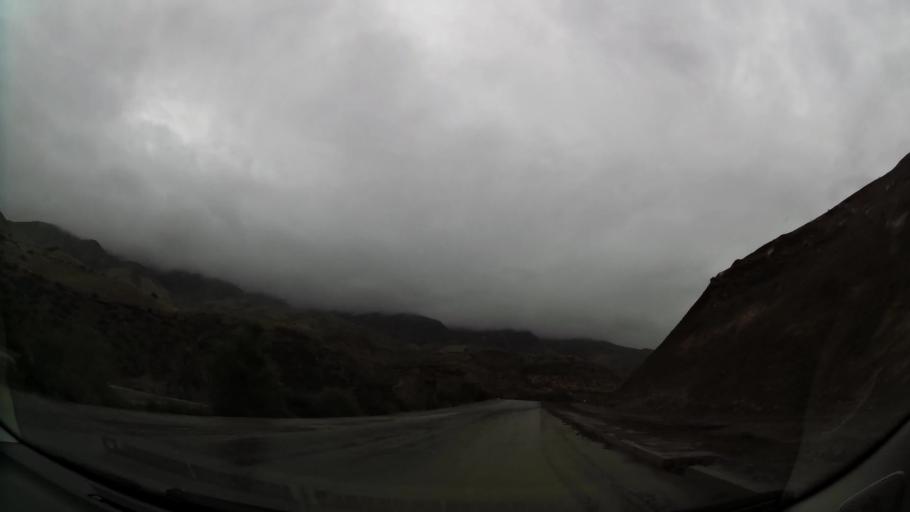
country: MA
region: Taza-Al Hoceima-Taounate
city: Imzourene
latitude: 35.0084
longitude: -3.8141
